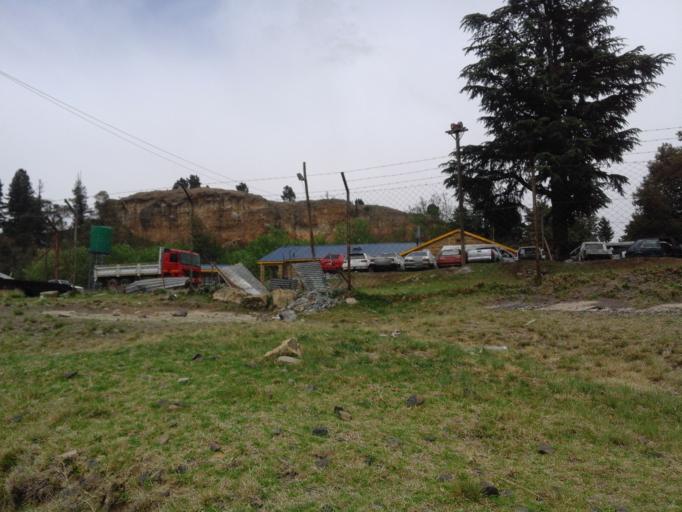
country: LS
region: Qacha's Nek
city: Qacha's Nek
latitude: -30.1199
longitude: 28.6893
